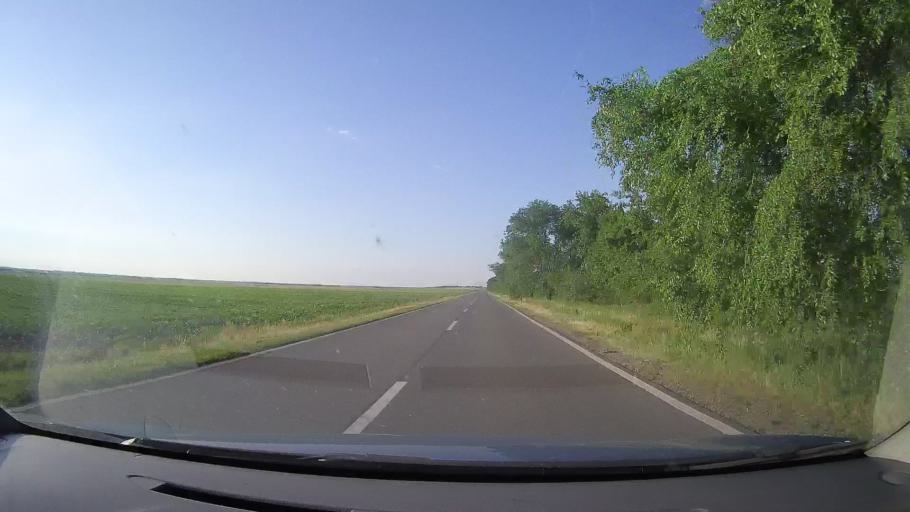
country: RS
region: Autonomna Pokrajina Vojvodina
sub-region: Juznobanatski Okrug
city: Vrsac
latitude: 45.1808
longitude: 21.2958
